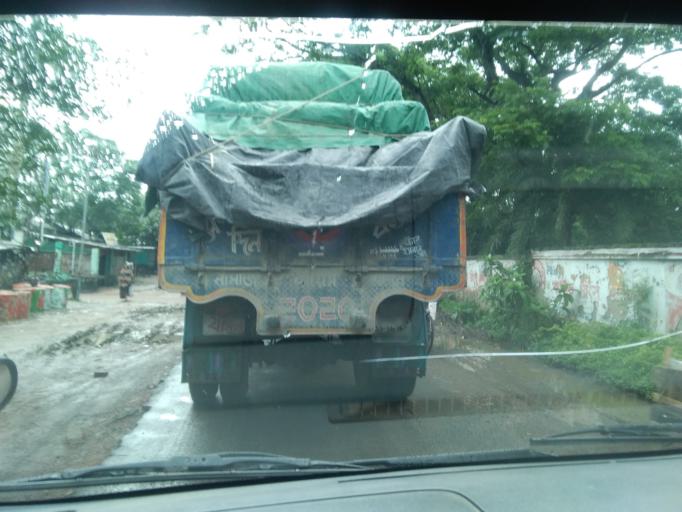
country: IN
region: West Bengal
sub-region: North 24 Parganas
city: Taki
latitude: 22.3460
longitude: 89.1042
